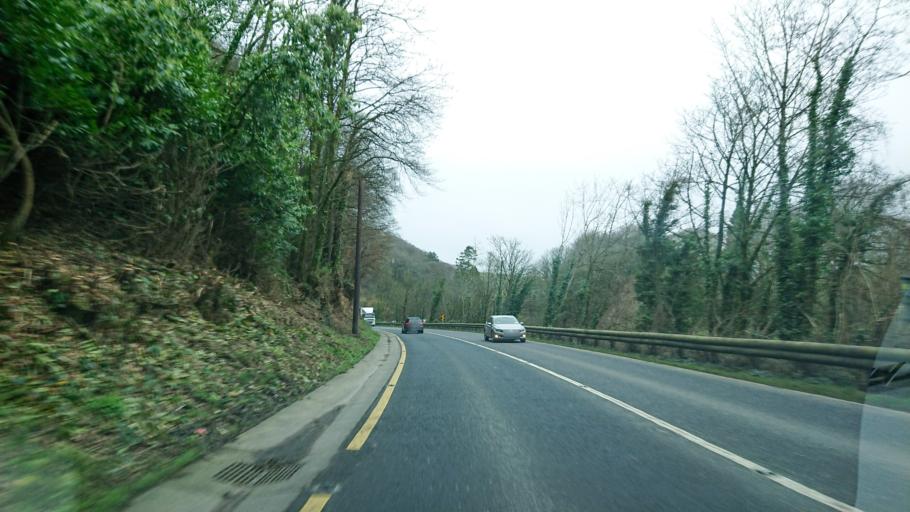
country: IE
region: Munster
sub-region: County Cork
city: Bandon
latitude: 51.7670
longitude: -8.6782
